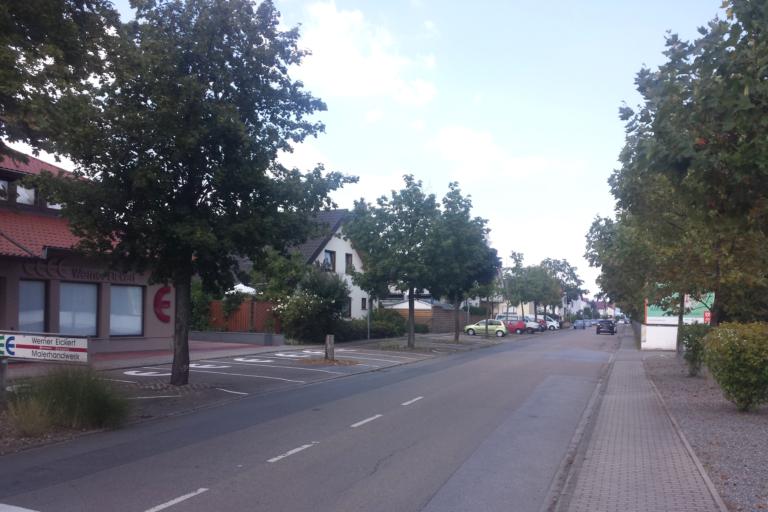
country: DE
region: Baden-Wuerttemberg
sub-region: Karlsruhe Region
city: Hemsbach
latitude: 49.5865
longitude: 8.6455
